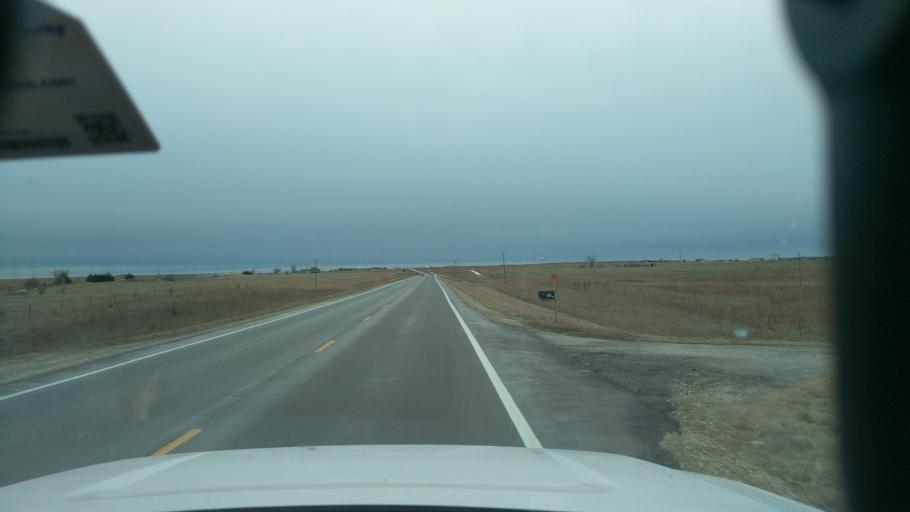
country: US
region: Kansas
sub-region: Dickinson County
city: Herington
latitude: 38.7035
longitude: -96.9294
